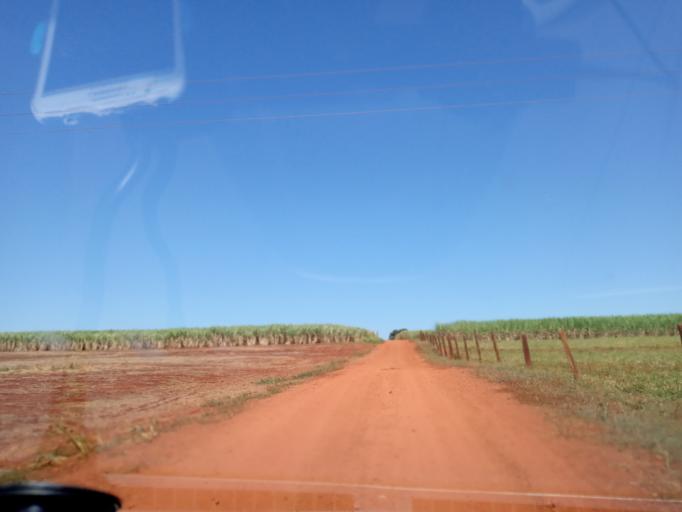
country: BR
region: Goias
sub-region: Itumbiara
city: Itumbiara
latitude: -18.4409
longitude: -49.1450
